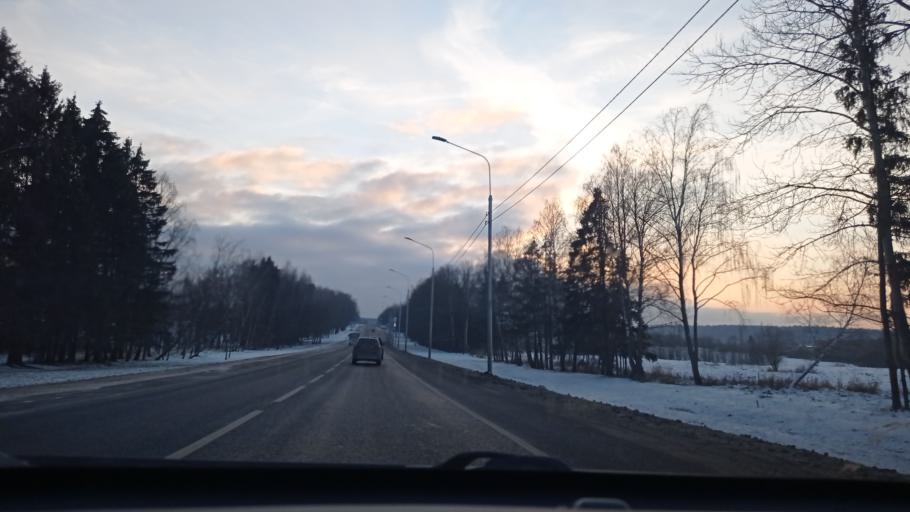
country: RU
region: Moskovskaya
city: Troitsk
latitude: 55.2893
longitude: 37.1268
